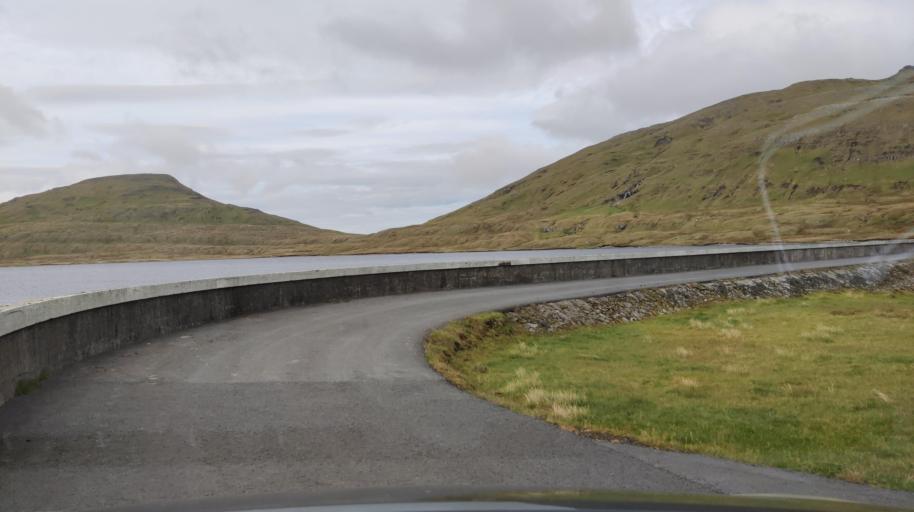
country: FO
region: Streymoy
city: Vestmanna
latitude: 62.1640
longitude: -7.0833
